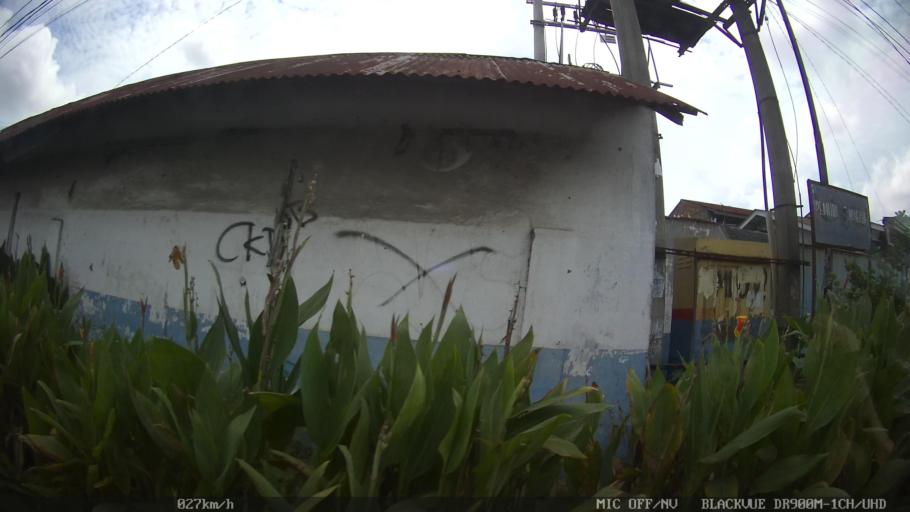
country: ID
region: North Sumatra
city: Medan
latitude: 3.6065
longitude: 98.7474
